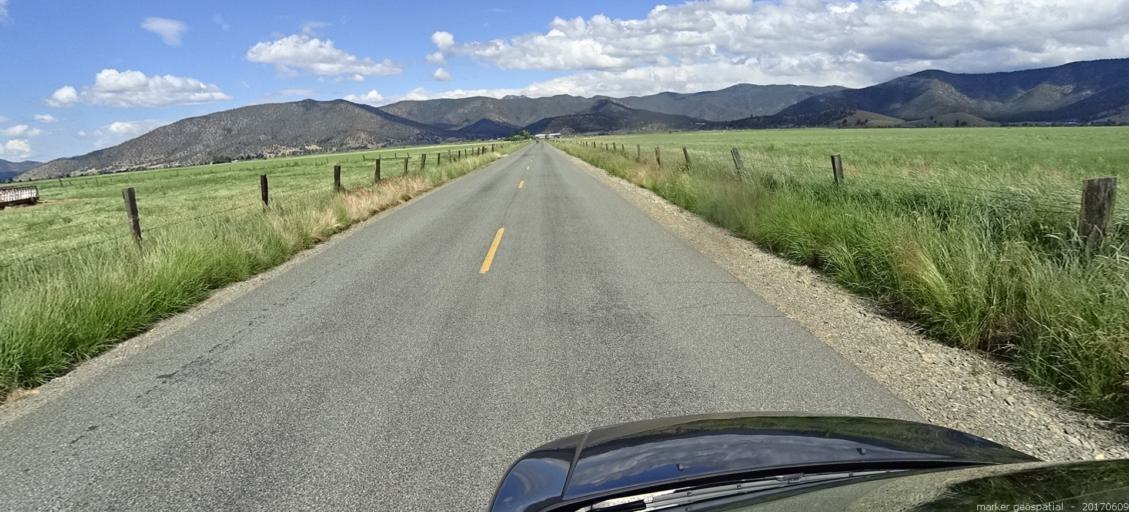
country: US
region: California
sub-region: Siskiyou County
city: Yreka
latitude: 41.4883
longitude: -122.8708
